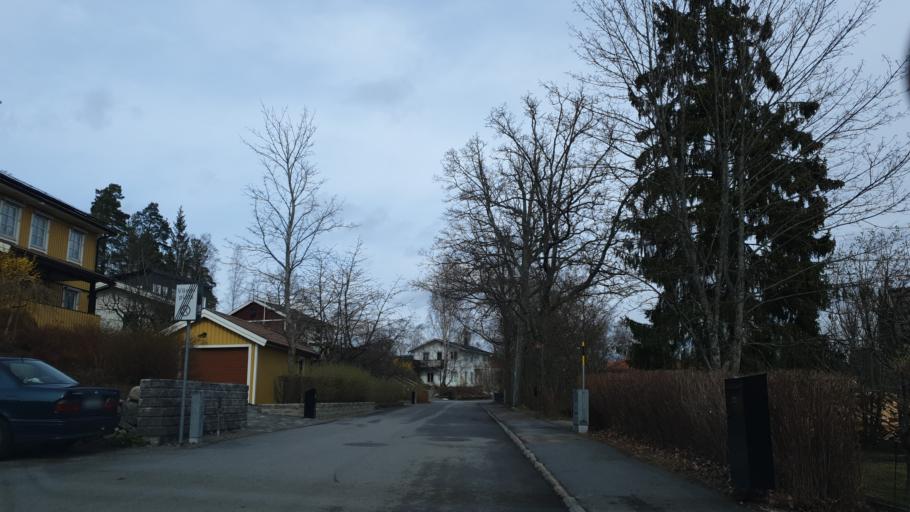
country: SE
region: Stockholm
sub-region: Nacka Kommun
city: Boo
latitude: 59.3270
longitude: 18.2746
